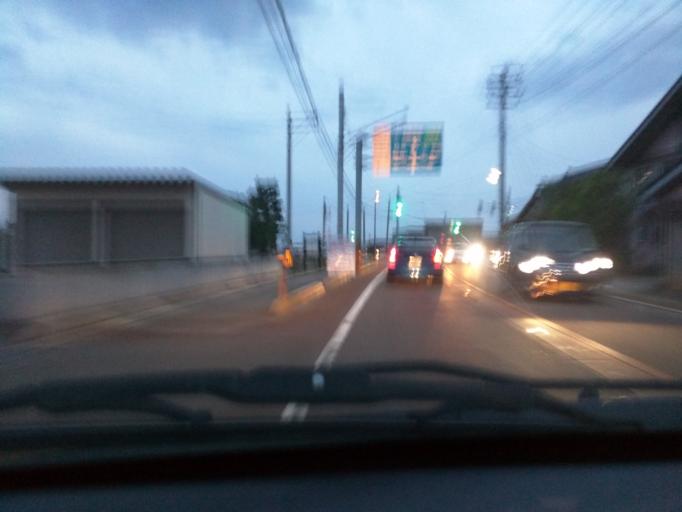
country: JP
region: Niigata
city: Kashiwazaki
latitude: 37.3430
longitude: 138.6120
